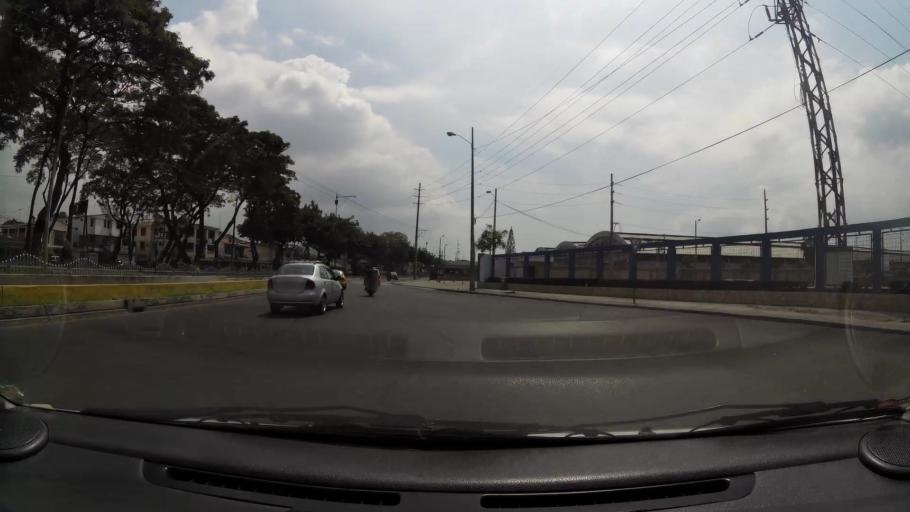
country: EC
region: Guayas
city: Guayaquil
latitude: -2.2311
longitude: -79.8901
